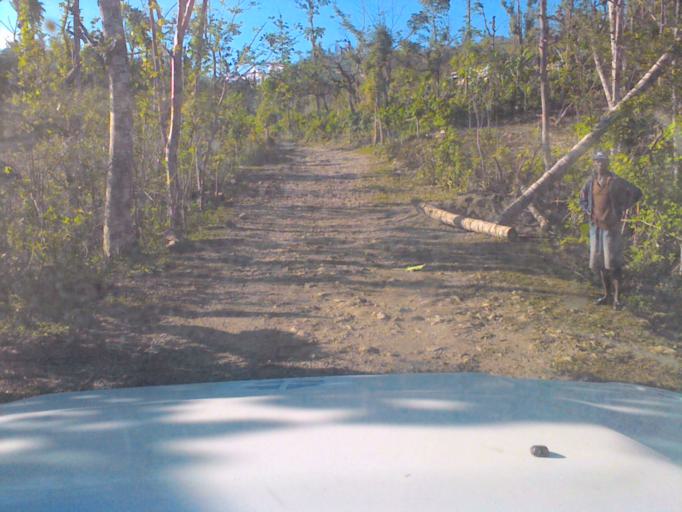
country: HT
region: Grandans
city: Jeremie
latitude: 18.5183
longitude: -74.0825
